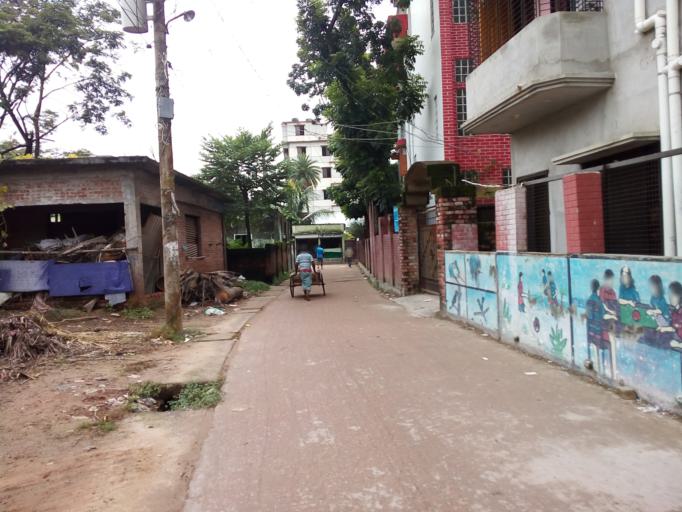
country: BD
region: Dhaka
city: Tungi
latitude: 23.8425
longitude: 90.2513
